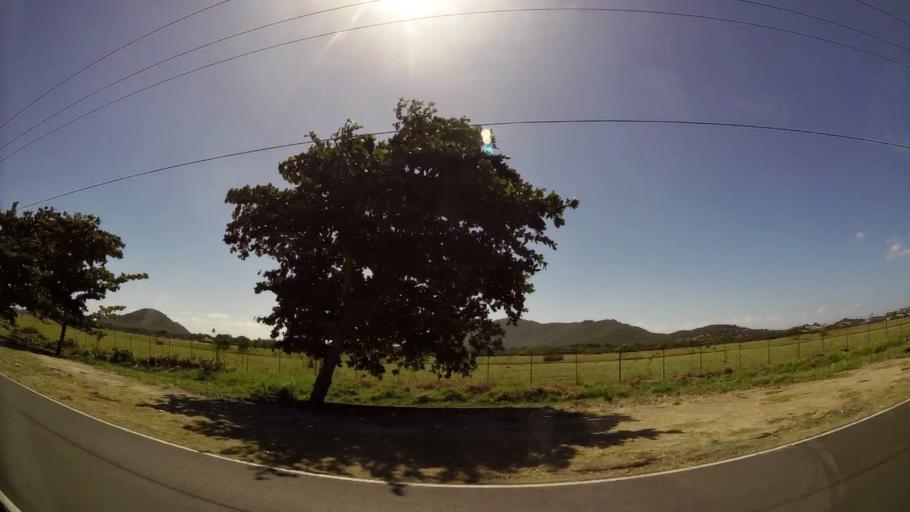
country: LC
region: Vieux-Fort
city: Vieux Fort
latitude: 13.7356
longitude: -60.9432
